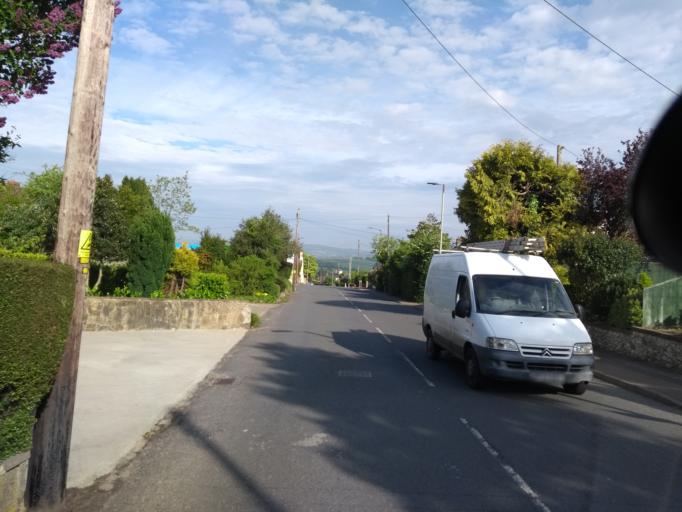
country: GB
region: England
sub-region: Devon
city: Axminster
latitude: 50.7789
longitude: -2.9874
